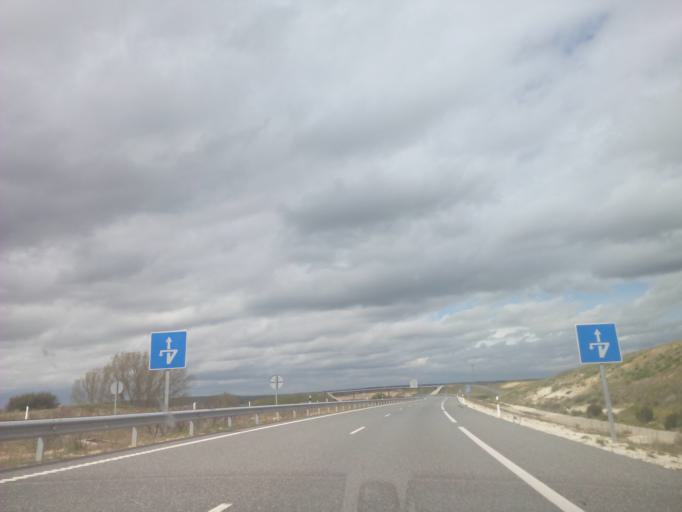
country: ES
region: Castille and Leon
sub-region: Provincia de Salamanca
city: Pelabravo
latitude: 40.9369
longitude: -5.5936
